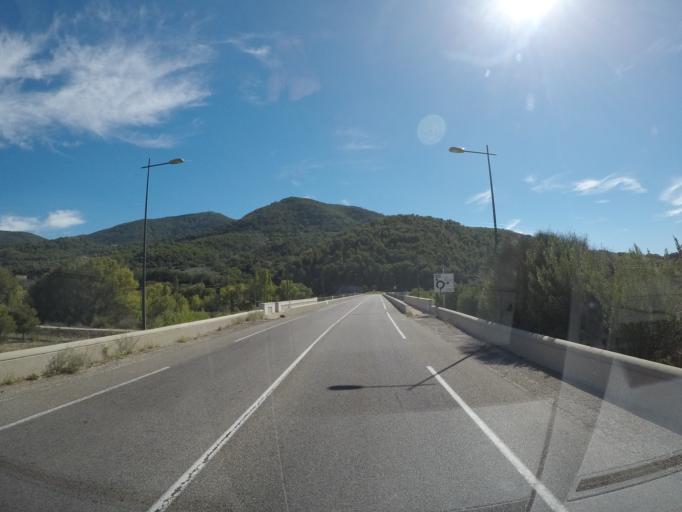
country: FR
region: Rhone-Alpes
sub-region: Departement de la Drome
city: Nyons
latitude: 44.3489
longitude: 5.1185
